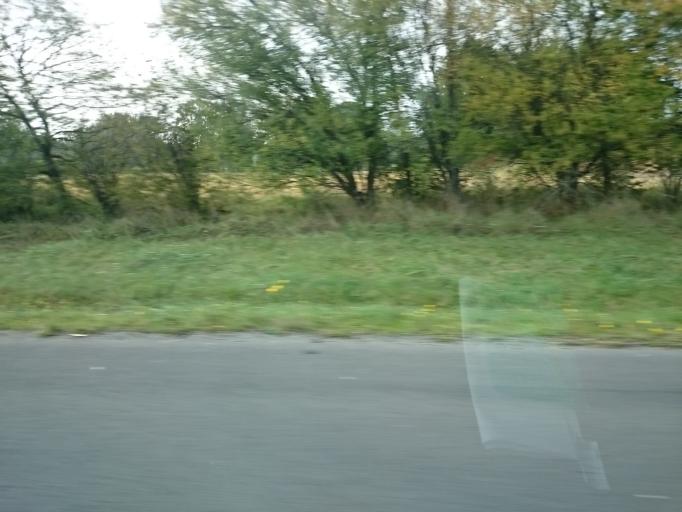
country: FR
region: Brittany
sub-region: Departement d'Ille-et-Vilaine
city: Laille
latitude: 47.9944
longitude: -1.6950
